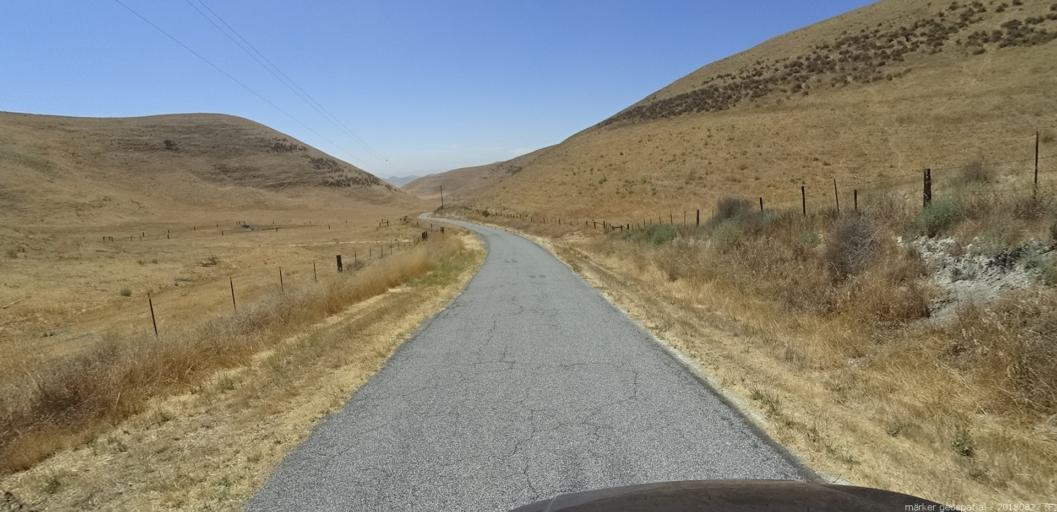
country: US
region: California
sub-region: Monterey County
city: King City
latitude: 36.1562
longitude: -120.8651
